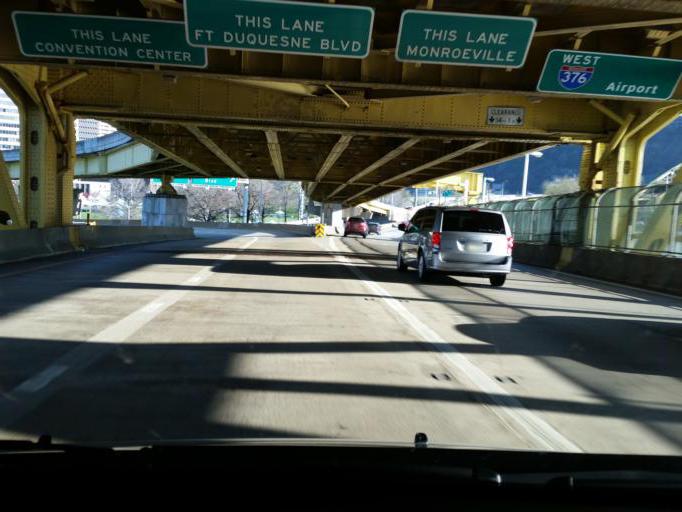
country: US
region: Pennsylvania
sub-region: Allegheny County
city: Pittsburgh
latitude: 40.4438
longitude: -80.0090
